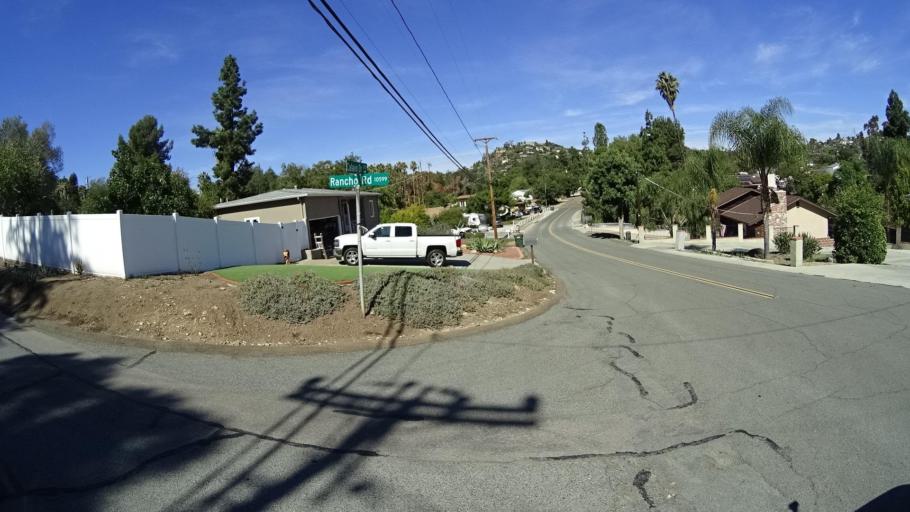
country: US
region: California
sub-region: San Diego County
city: Casa de Oro-Mount Helix
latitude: 32.7503
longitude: -116.9668
